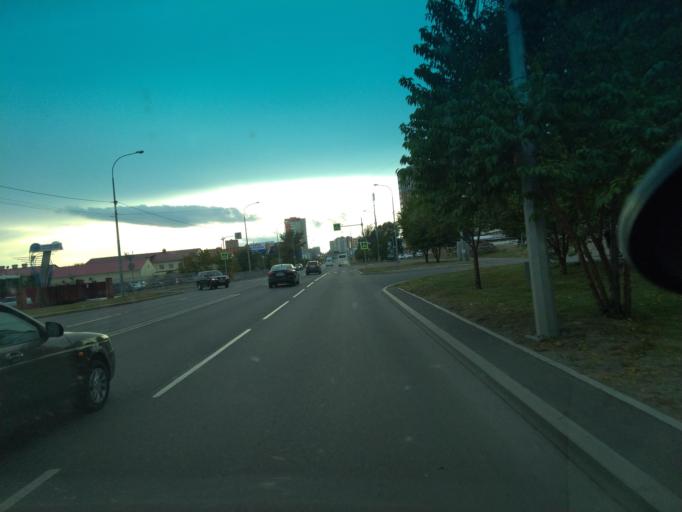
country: RU
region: Krasnoyarskiy
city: Krasnoyarsk
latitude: 56.0338
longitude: 92.9041
